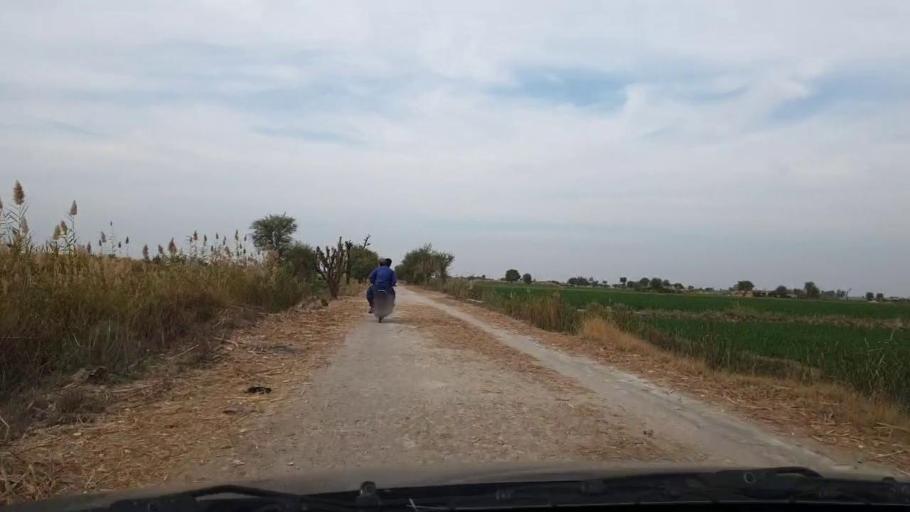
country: PK
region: Sindh
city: Khadro
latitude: 26.1652
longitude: 68.7301
